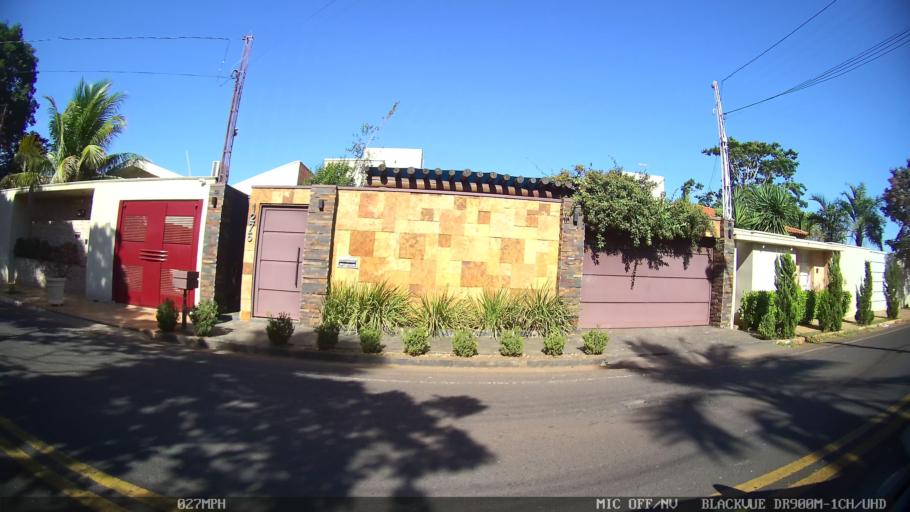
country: BR
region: Sao Paulo
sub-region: Olimpia
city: Olimpia
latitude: -20.7556
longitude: -48.9126
